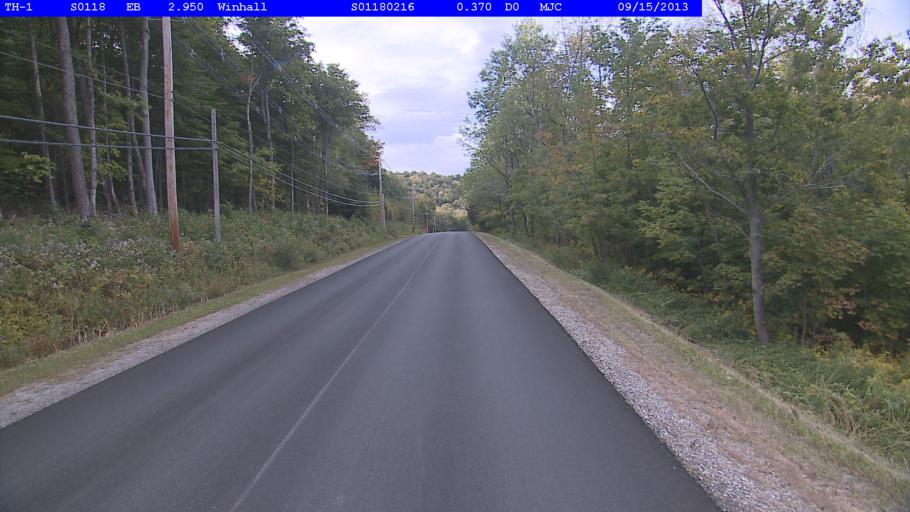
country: US
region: Vermont
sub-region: Bennington County
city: Manchester Center
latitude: 43.1204
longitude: -72.9118
